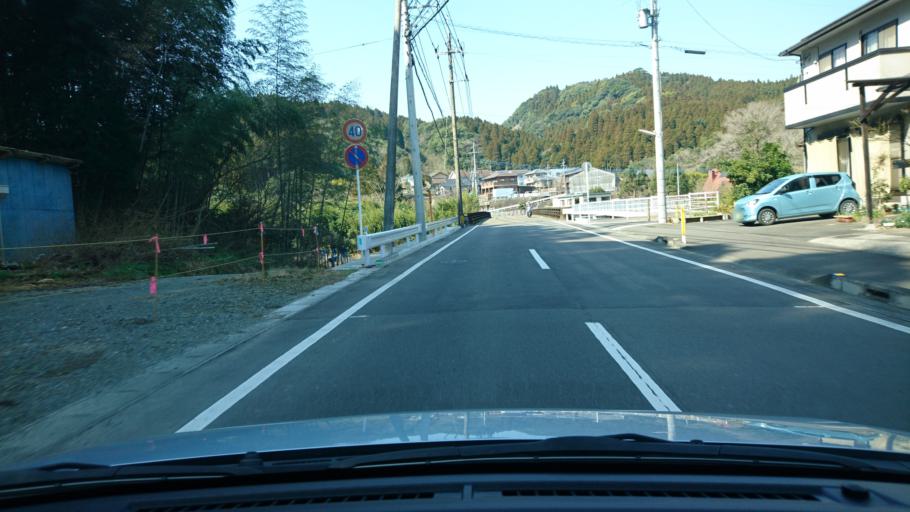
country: JP
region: Miyazaki
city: Miyazaki-shi
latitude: 31.8288
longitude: 131.4021
